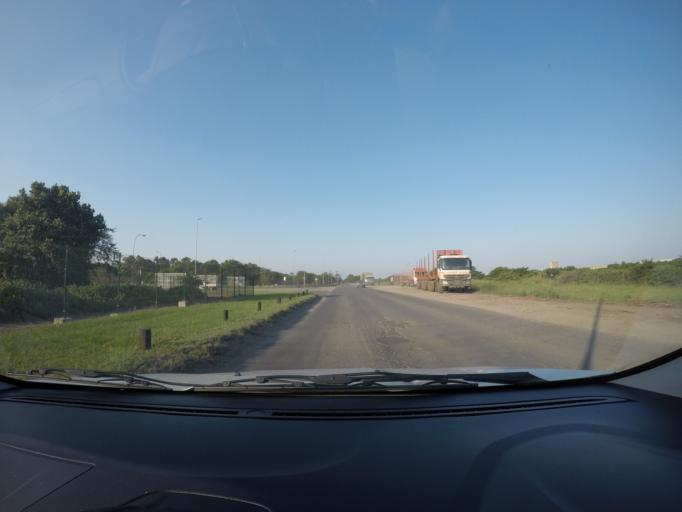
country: ZA
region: KwaZulu-Natal
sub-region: uThungulu District Municipality
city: Richards Bay
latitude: -28.7635
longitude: 32.0005
